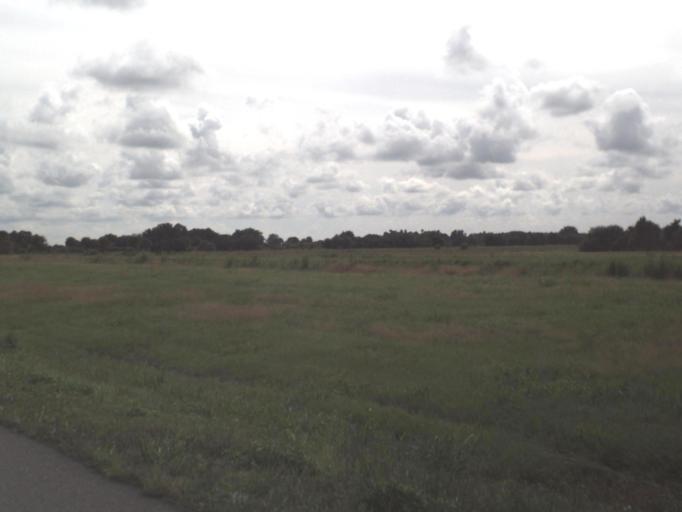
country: US
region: Florida
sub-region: Highlands County
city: Lake Placid
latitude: 27.2097
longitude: -81.1557
